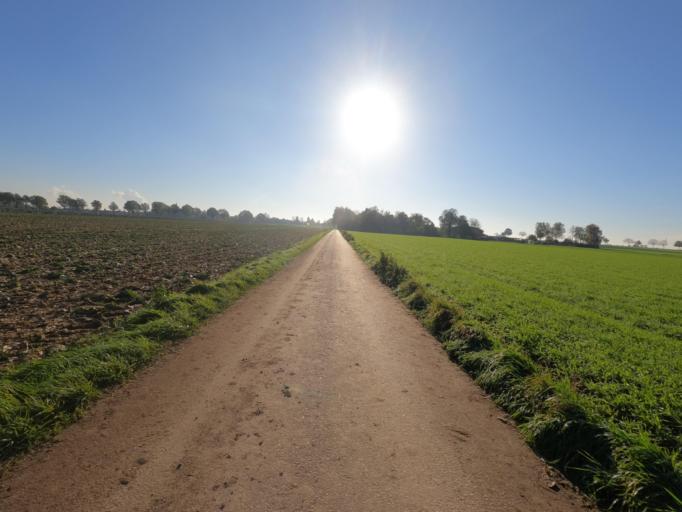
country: DE
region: North Rhine-Westphalia
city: Erkelenz
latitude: 51.0951
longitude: 6.3609
